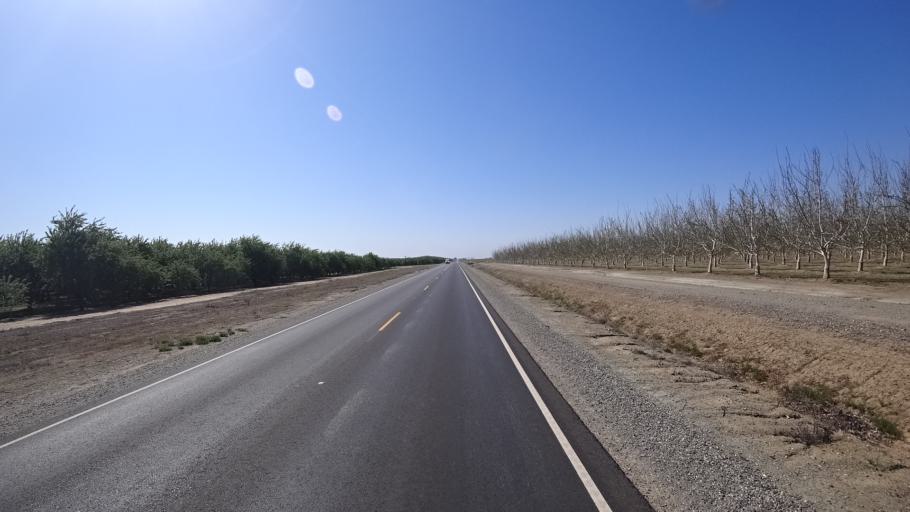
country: US
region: California
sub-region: Glenn County
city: Hamilton City
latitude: 39.6400
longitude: -122.0650
